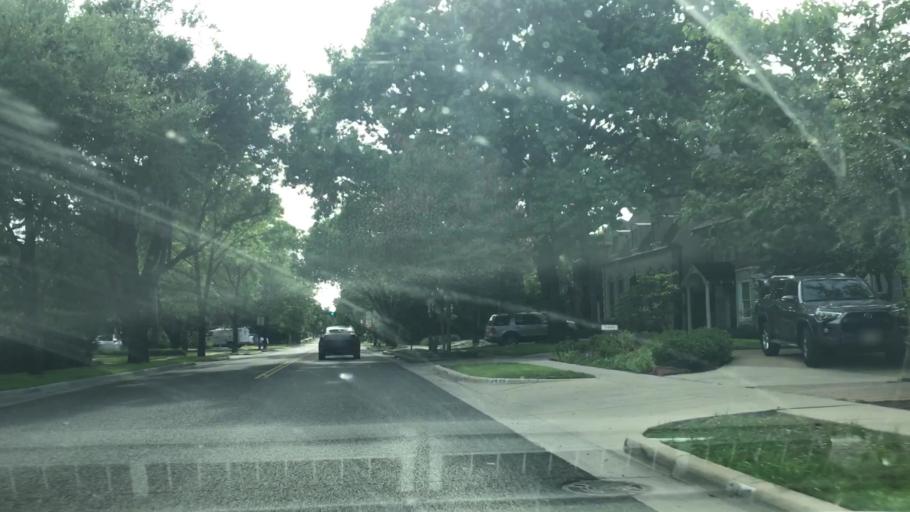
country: US
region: Texas
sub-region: Dallas County
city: Highland Park
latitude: 32.8366
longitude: -96.7890
